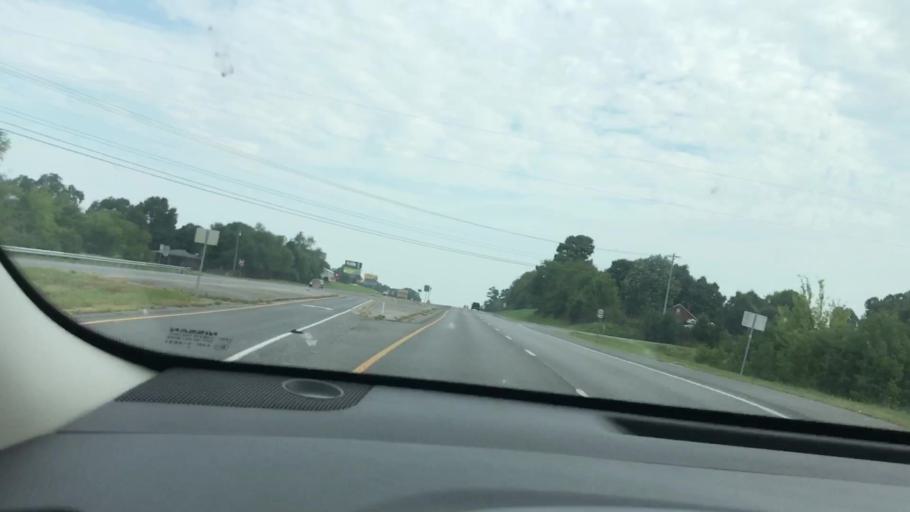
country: US
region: Kentucky
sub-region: Calloway County
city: Murray
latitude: 36.6756
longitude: -88.3024
